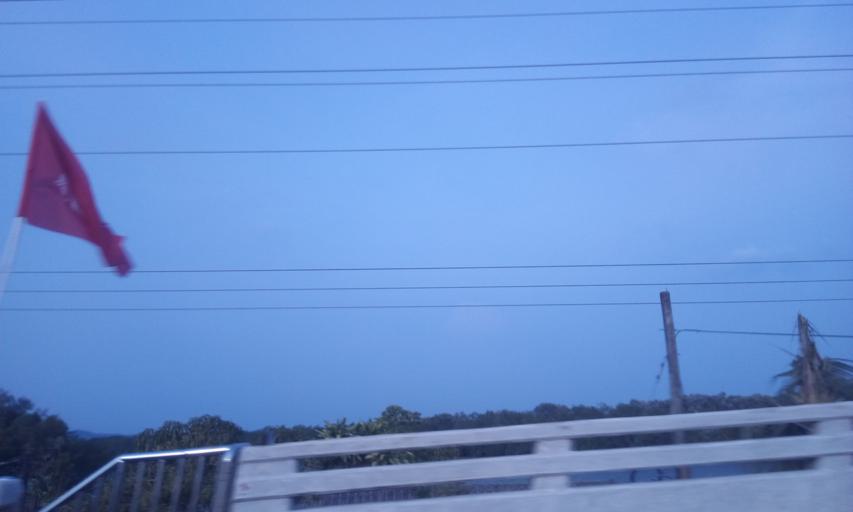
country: TH
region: Trat
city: Khao Saming
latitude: 12.3876
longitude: 102.3702
